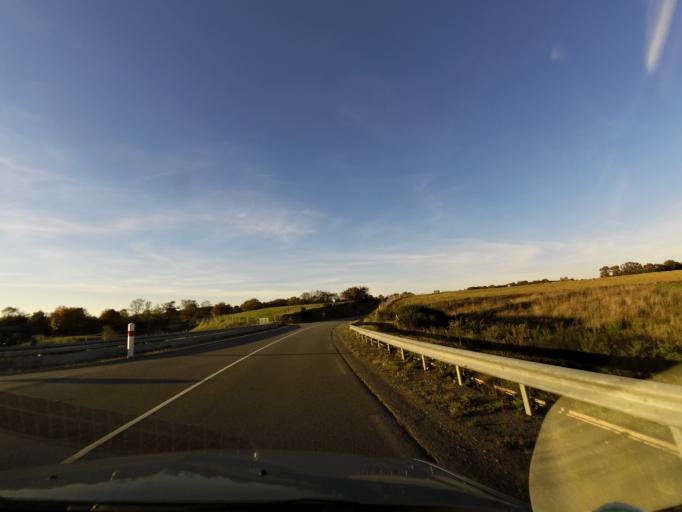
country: FR
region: Brittany
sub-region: Departement d'Ille-et-Vilaine
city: Crevin
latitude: 47.9166
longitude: -1.6782
